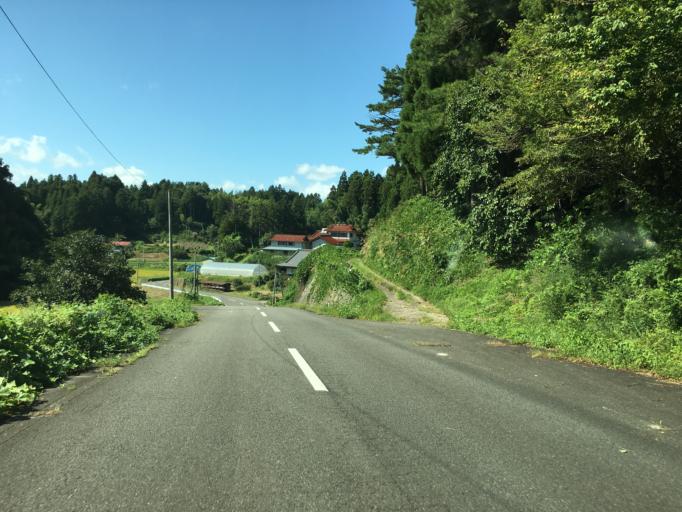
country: JP
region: Fukushima
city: Sukagawa
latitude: 37.2788
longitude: 140.4630
